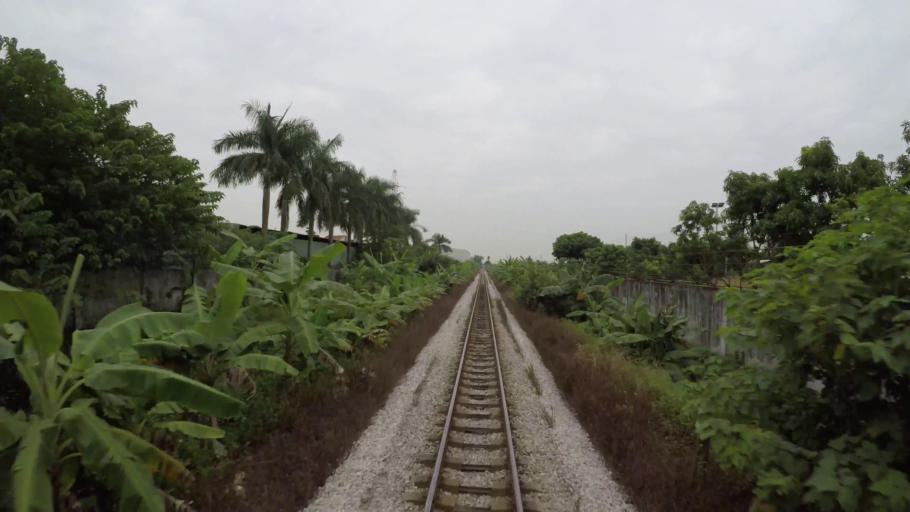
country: VN
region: Hai Phong
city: An Duong
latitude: 20.8984
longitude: 106.5813
